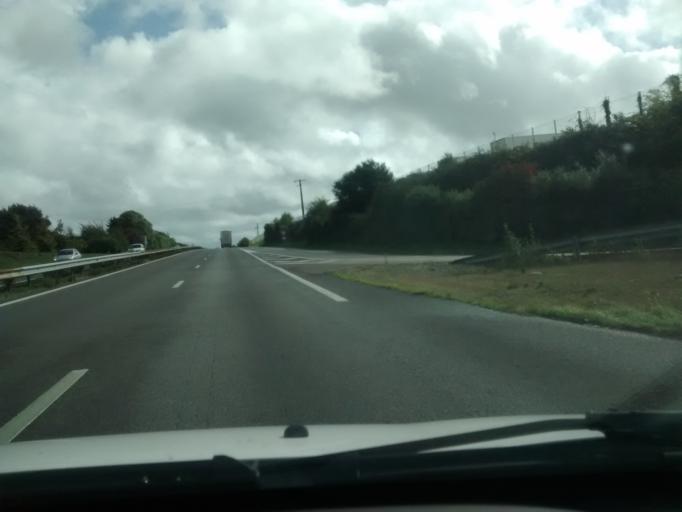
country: FR
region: Brittany
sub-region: Departement d'Ille-et-Vilaine
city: Noyal-sur-Vilaine
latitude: 48.1102
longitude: -1.5327
